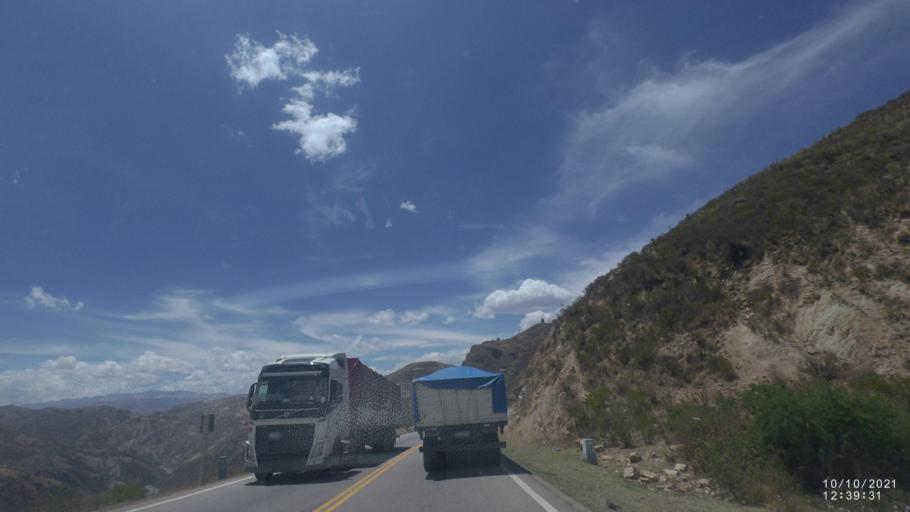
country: BO
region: Cochabamba
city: Irpa Irpa
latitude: -17.6447
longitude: -66.3932
